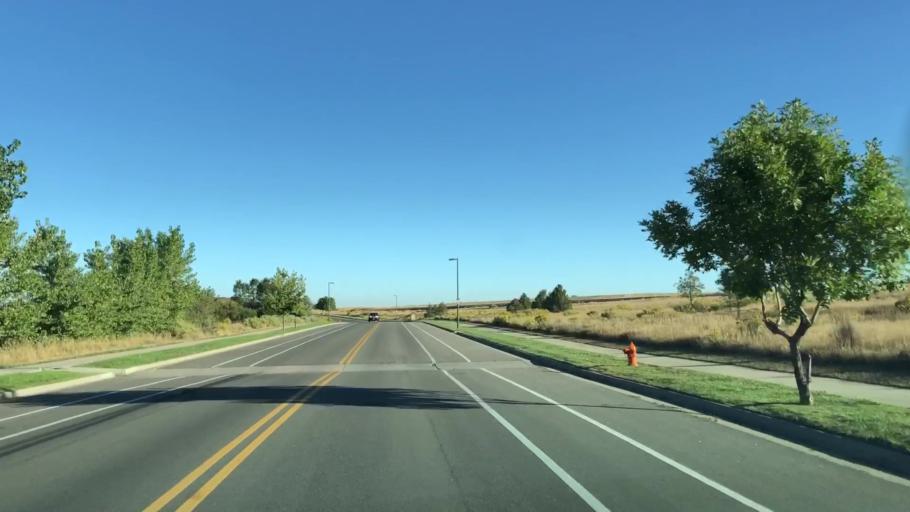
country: US
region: Colorado
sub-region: Larimer County
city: Loveland
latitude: 40.4493
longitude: -105.0248
